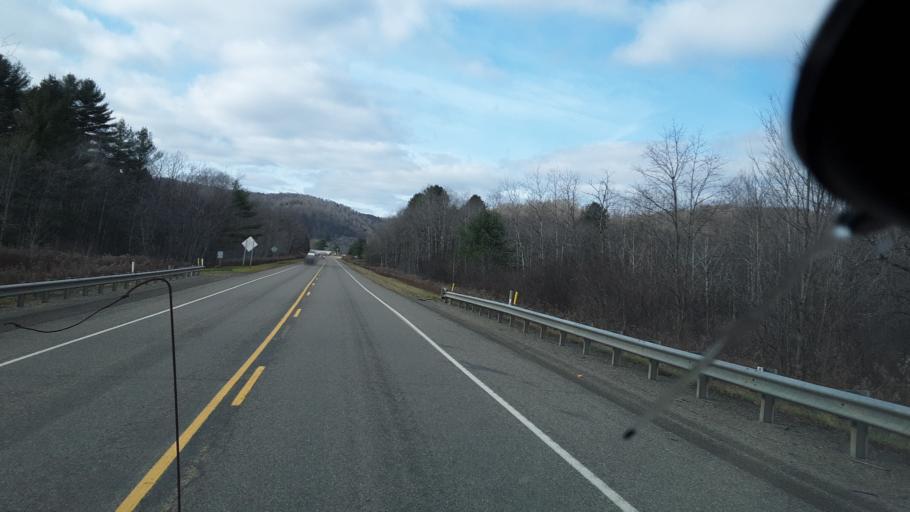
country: US
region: Pennsylvania
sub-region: Potter County
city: Galeton
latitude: 41.7771
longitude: -77.7152
